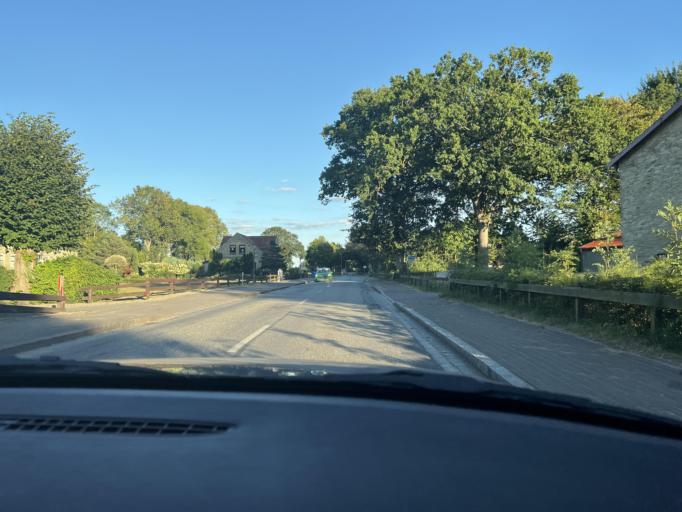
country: DE
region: Schleswig-Holstein
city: Kleve
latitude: 54.2946
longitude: 9.1288
